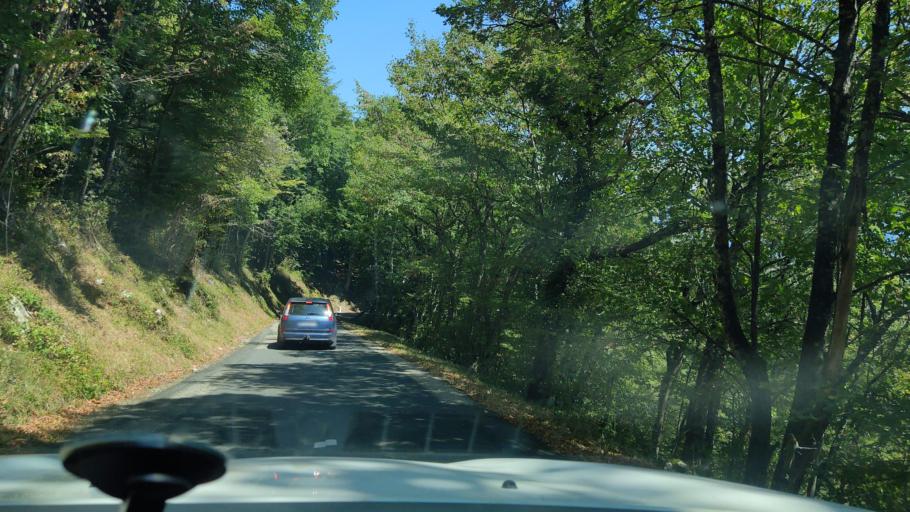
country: FR
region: Rhone-Alpes
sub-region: Departement de la Savoie
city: Le Bourget-du-Lac
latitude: 45.6569
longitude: 5.8425
